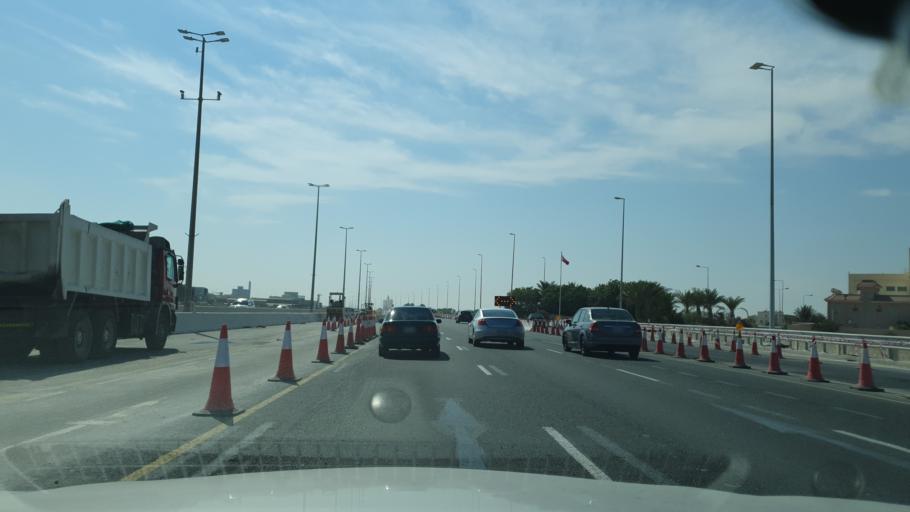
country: BH
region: Manama
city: Jidd Hafs
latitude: 26.1998
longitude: 50.5094
